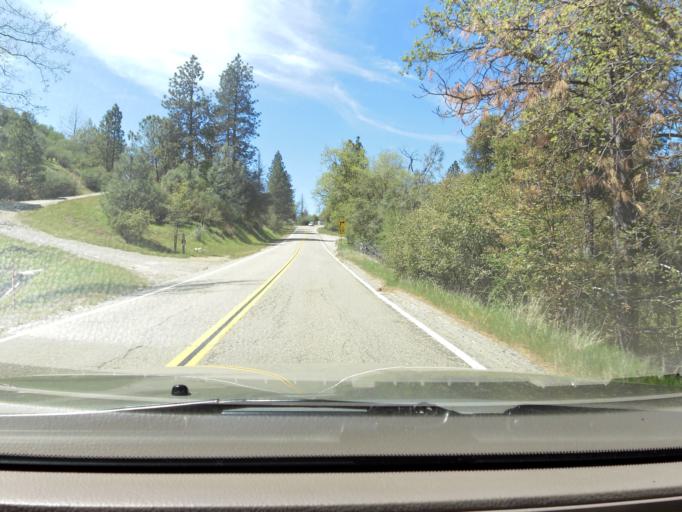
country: US
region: California
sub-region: Madera County
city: Oakhurst
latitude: 37.2484
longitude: -119.5636
